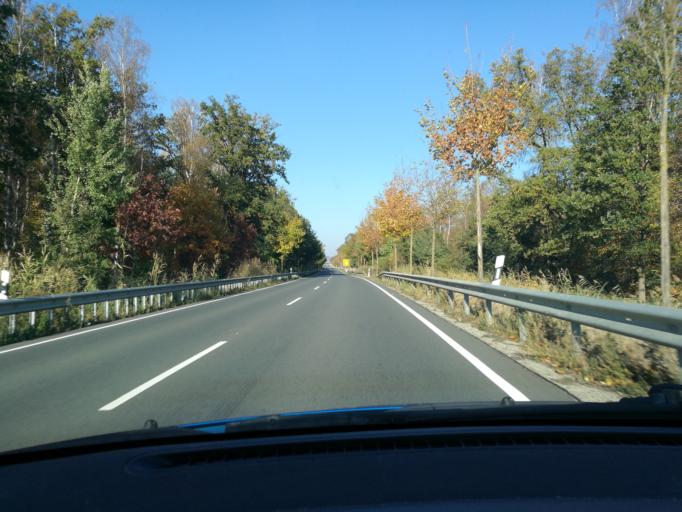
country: DE
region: Mecklenburg-Vorpommern
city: Domitz
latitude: 53.1282
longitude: 11.2195
